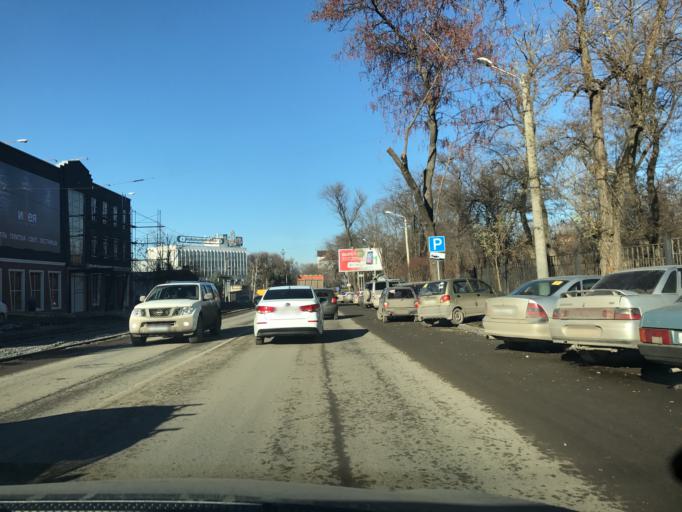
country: RU
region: Rostov
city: Rostov-na-Donu
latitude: 47.2414
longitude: 39.7523
